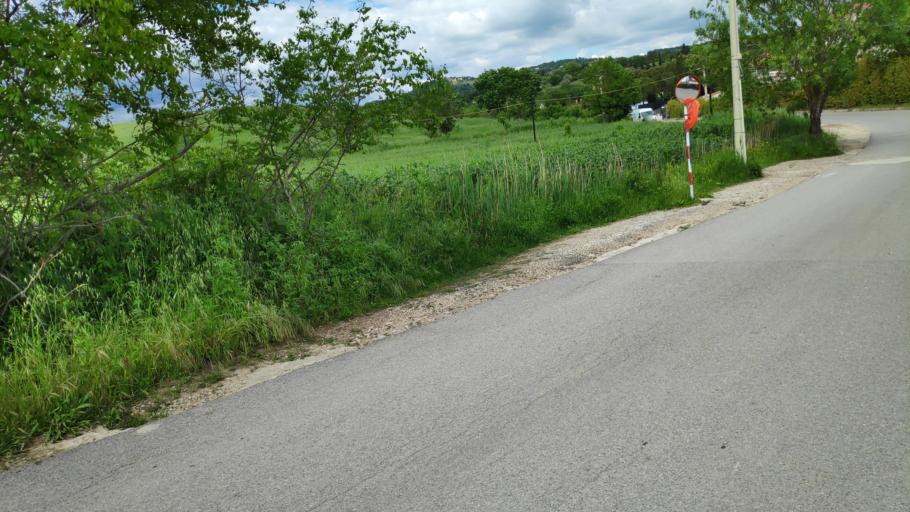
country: IT
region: Tuscany
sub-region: Provincia di Grosseto
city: Manciano
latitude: 42.6588
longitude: 11.5156
